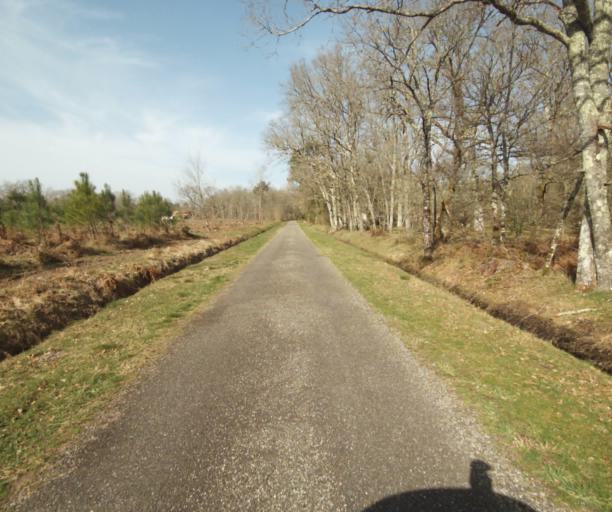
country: FR
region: Aquitaine
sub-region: Departement des Landes
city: Roquefort
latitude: 44.1479
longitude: -0.2058
